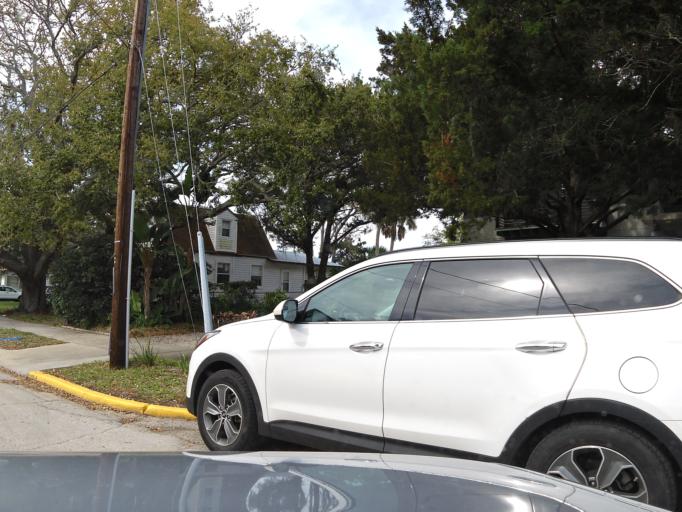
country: US
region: Florida
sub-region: Saint Johns County
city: Saint Augustine
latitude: 29.9163
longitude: -81.3149
